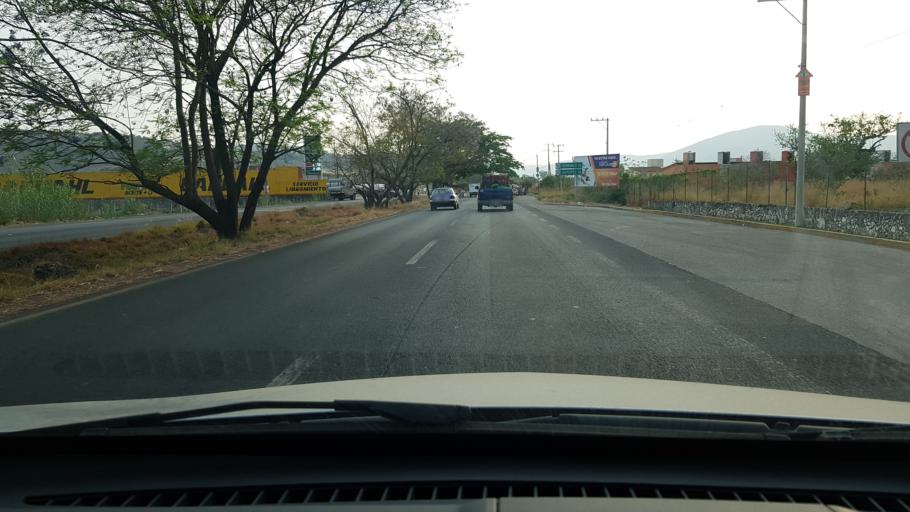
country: MX
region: Morelos
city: Yautepec
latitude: 18.8758
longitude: -99.0558
